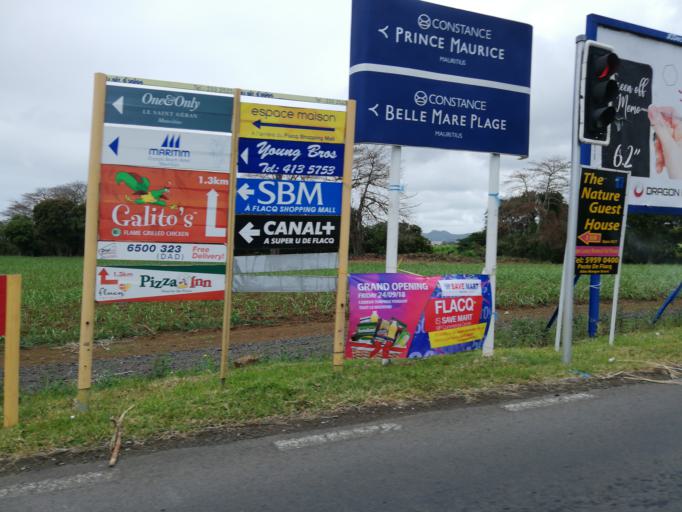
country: MU
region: Flacq
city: Centre de Flacq
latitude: -20.1782
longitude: 57.7193
